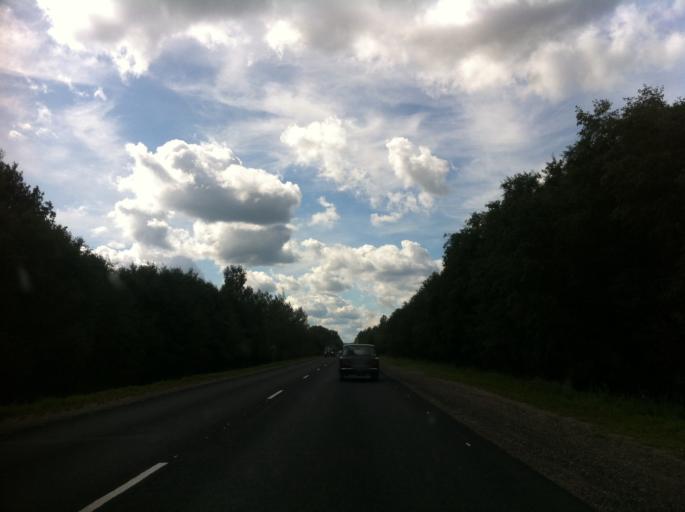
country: RU
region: Pskov
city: Izborsk
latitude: 57.7148
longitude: 27.9121
